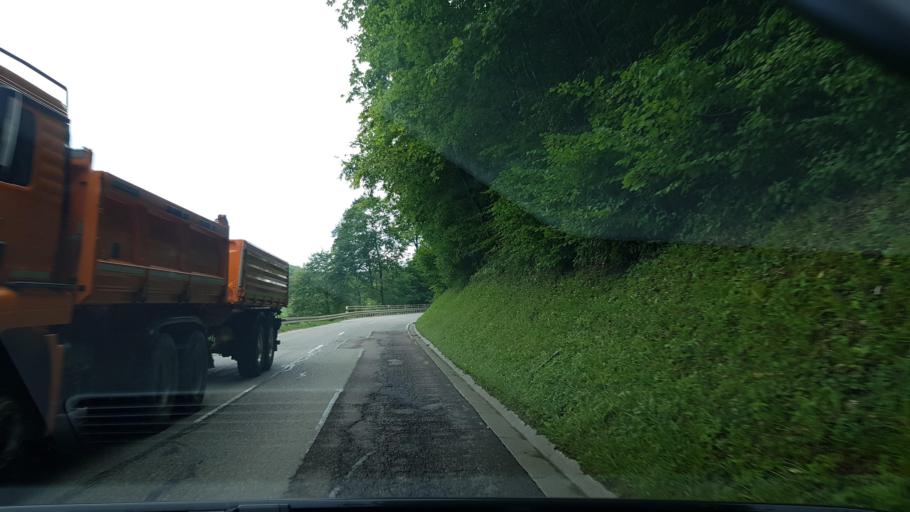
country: DE
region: Baden-Wuerttemberg
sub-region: Tuebingen Region
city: Grabenstetten
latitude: 48.5328
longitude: 9.4924
